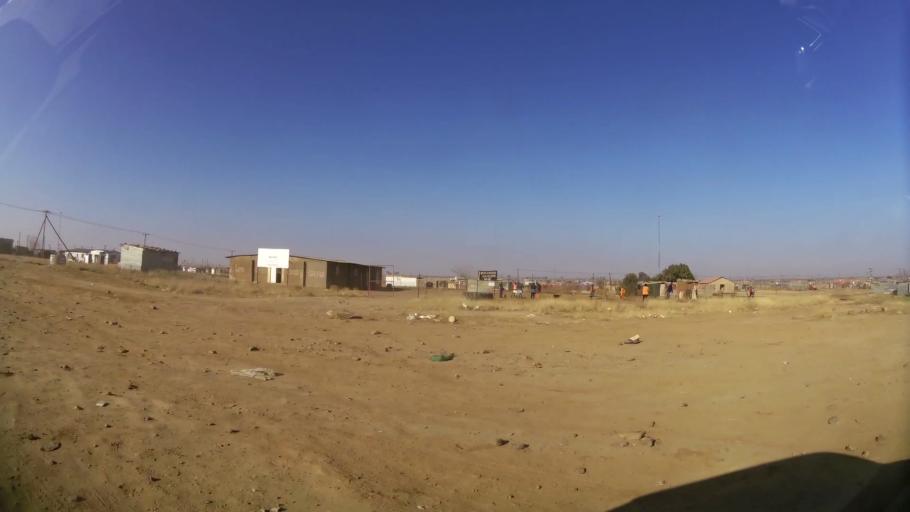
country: ZA
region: Orange Free State
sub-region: Mangaung Metropolitan Municipality
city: Bloemfontein
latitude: -29.2047
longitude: 26.2487
